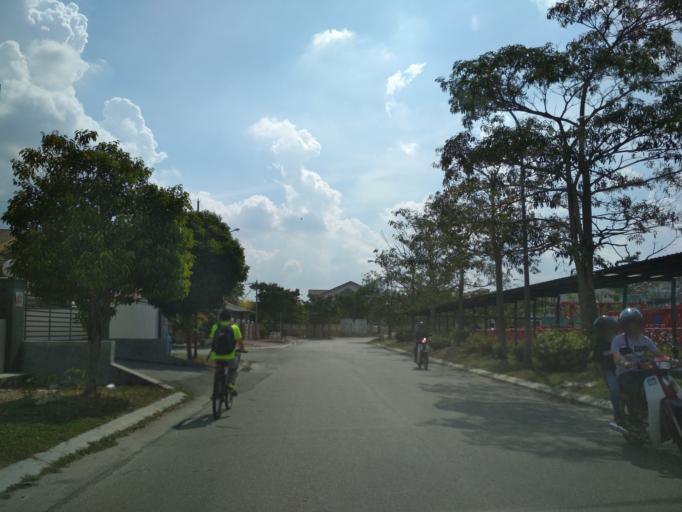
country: MY
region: Perak
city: Kampar
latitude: 4.3305
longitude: 101.1330
